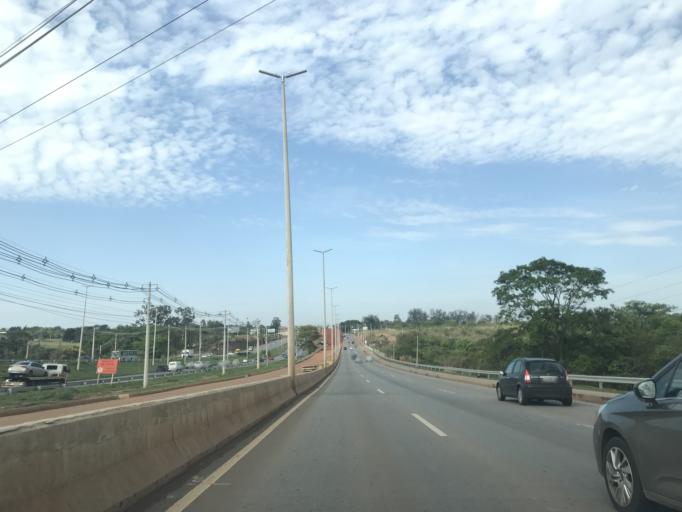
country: BR
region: Federal District
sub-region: Brasilia
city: Brasilia
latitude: -15.7050
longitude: -47.8900
